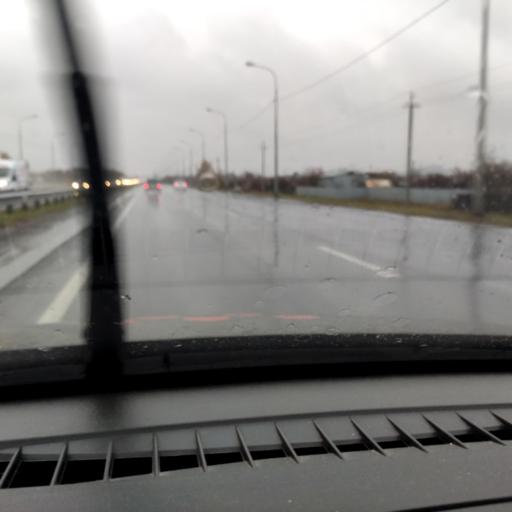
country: RU
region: Samara
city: Tol'yatti
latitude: 53.5748
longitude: 49.4436
